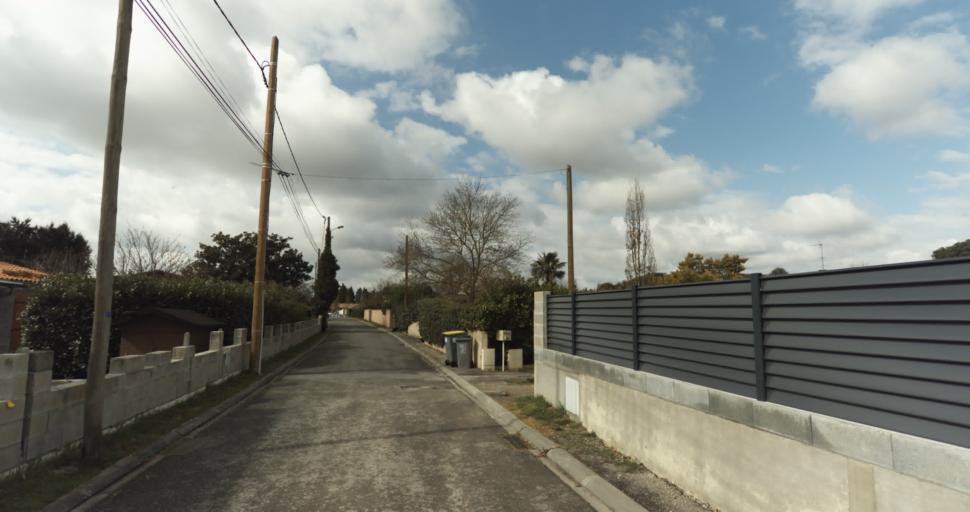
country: FR
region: Midi-Pyrenees
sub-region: Departement de la Haute-Garonne
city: Auterive
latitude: 43.3520
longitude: 1.4658
